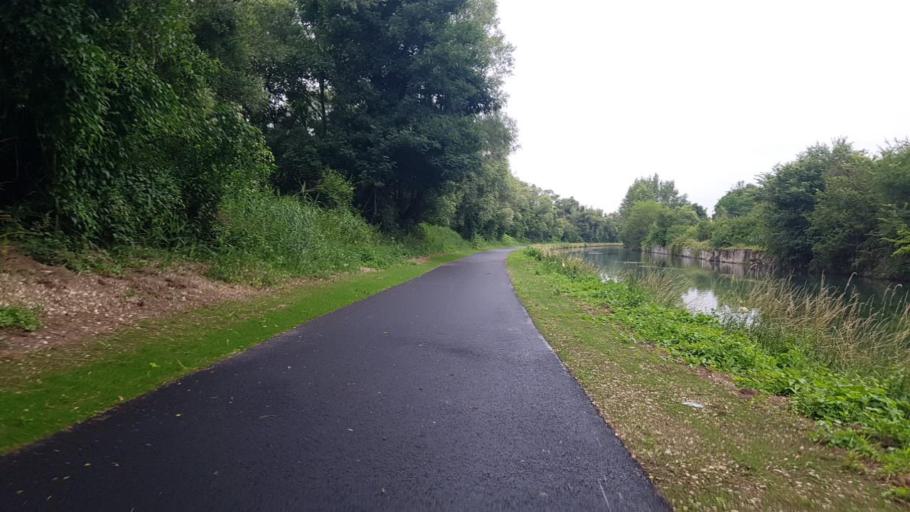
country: FR
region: Champagne-Ardenne
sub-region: Departement de la Marne
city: Vitry-le-Francois
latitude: 48.7760
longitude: 4.5434
